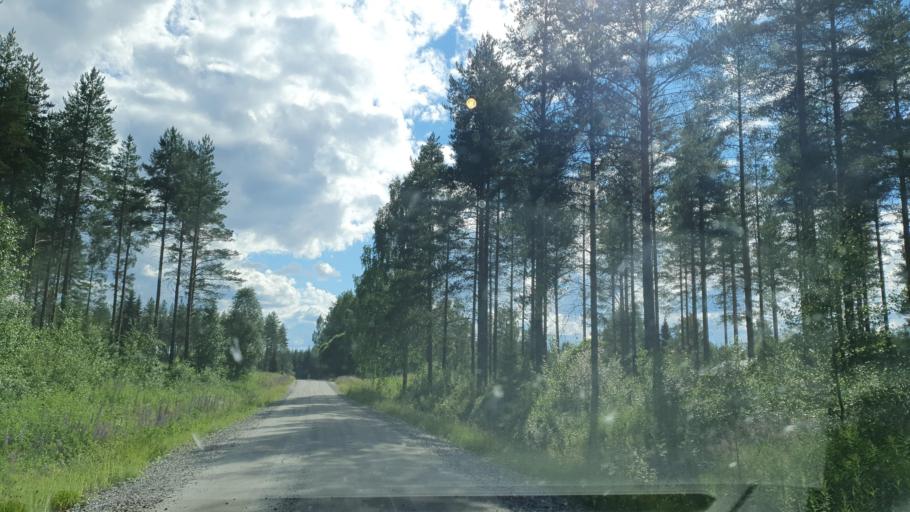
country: FI
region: Kainuu
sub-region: Kehys-Kainuu
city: Kuhmo
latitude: 64.1365
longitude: 29.6704
